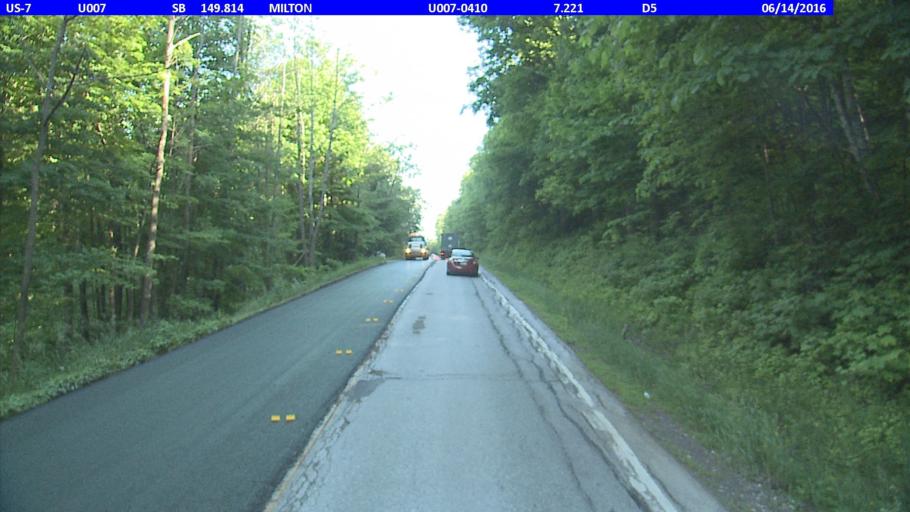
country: US
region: Vermont
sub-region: Chittenden County
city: Milton
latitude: 44.6705
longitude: -73.1120
